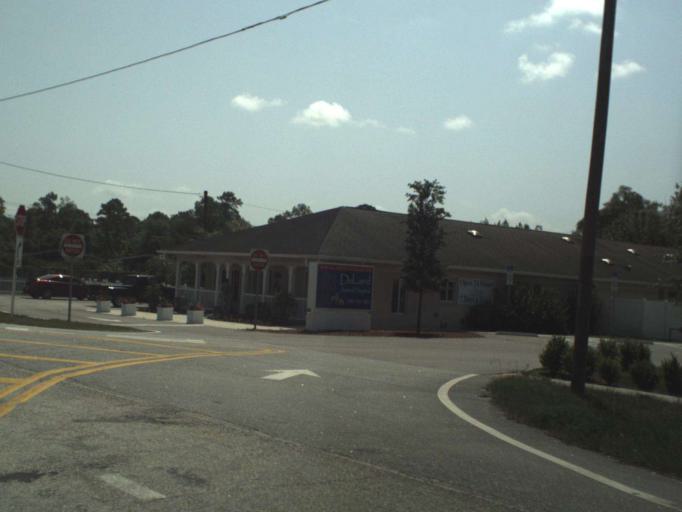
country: US
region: Florida
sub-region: Volusia County
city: North DeLand
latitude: 29.0635
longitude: -81.2625
